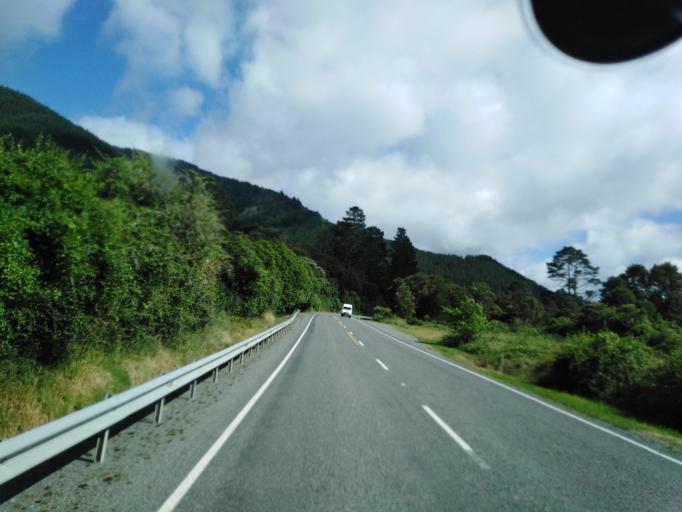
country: NZ
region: Nelson
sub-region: Nelson City
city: Nelson
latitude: -41.2914
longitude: 173.5729
